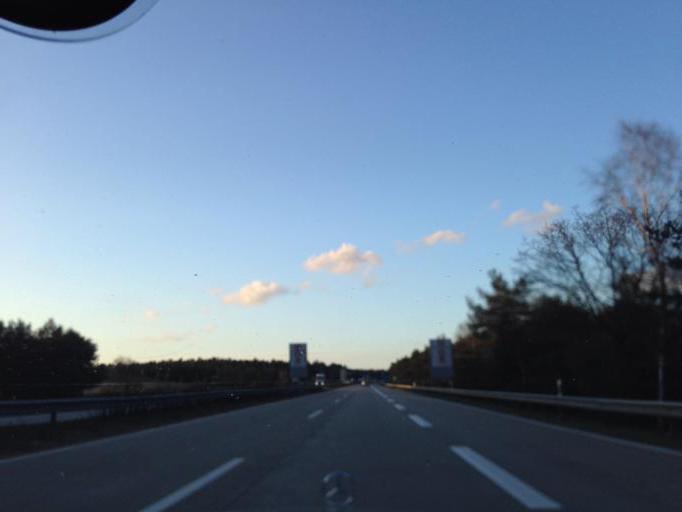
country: DE
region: Lower Saxony
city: Soltau
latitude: 53.0004
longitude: 9.9288
